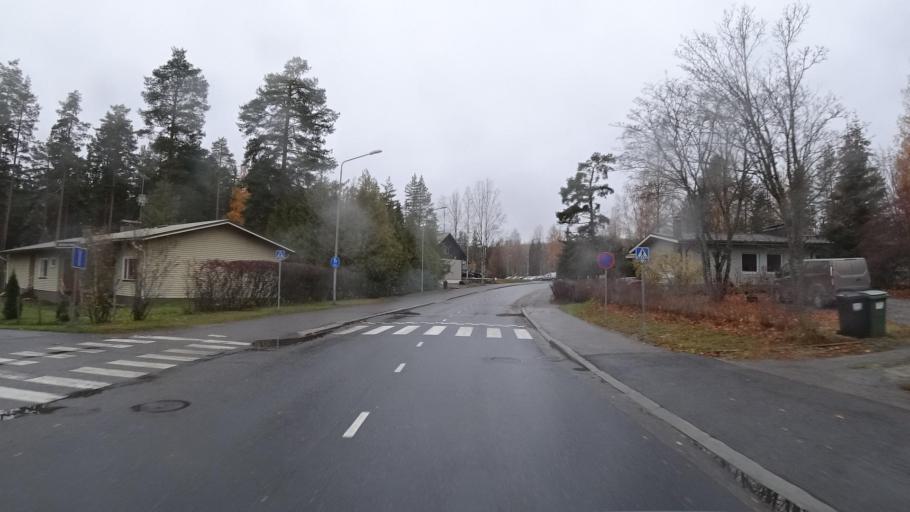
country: FI
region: Northern Savo
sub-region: Kuopio
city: Kuopio
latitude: 62.9231
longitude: 27.6820
